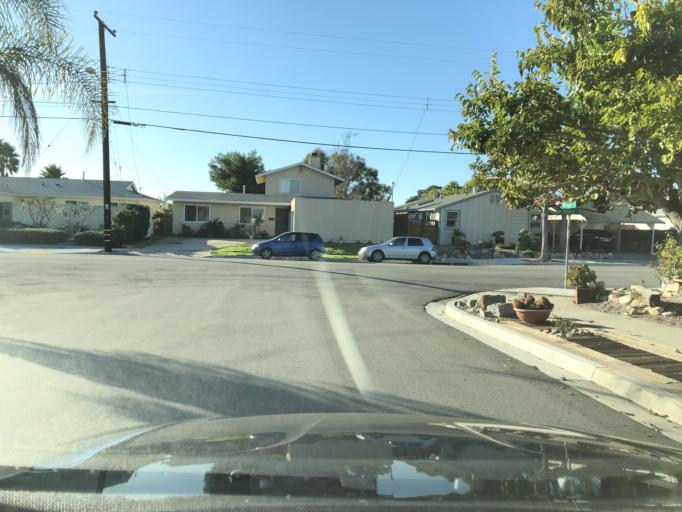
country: US
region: California
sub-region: San Diego County
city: La Jolla
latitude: 32.8206
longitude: -117.1962
